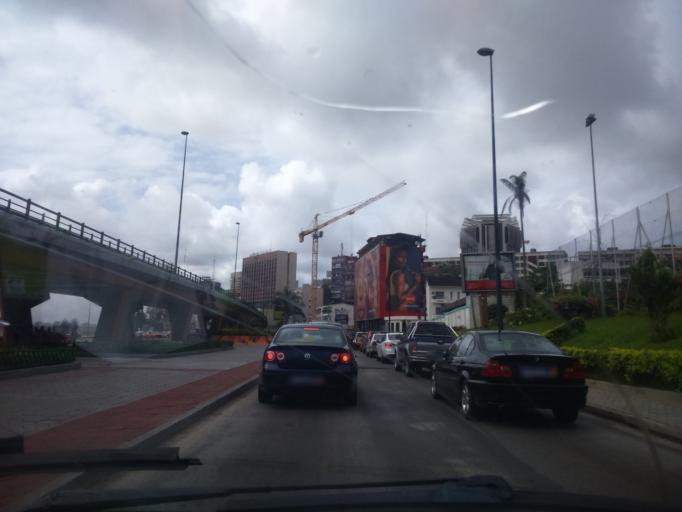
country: CI
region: Lagunes
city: Abidjan
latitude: 5.3252
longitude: -4.0159
